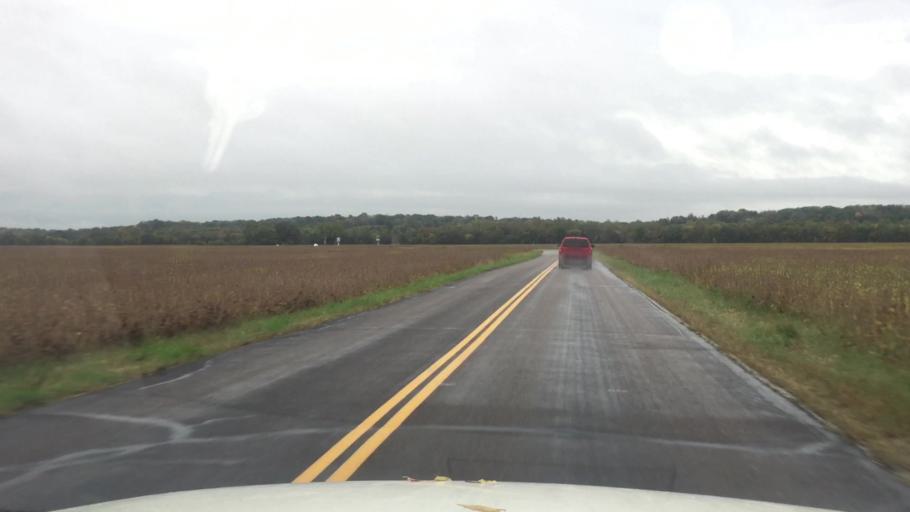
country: US
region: Missouri
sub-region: Boone County
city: Columbia
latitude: 38.8907
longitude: -92.4658
